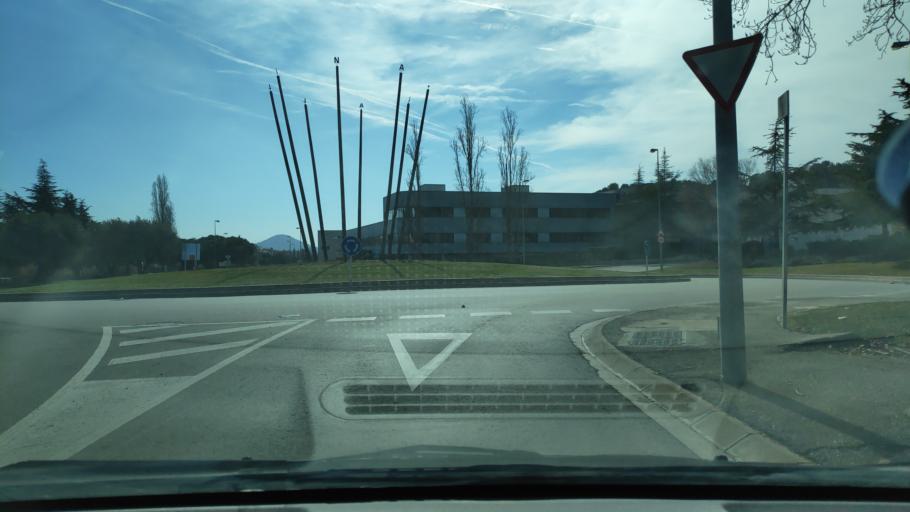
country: ES
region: Catalonia
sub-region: Provincia de Barcelona
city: Rubi
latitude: 41.5081
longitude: 2.0328
